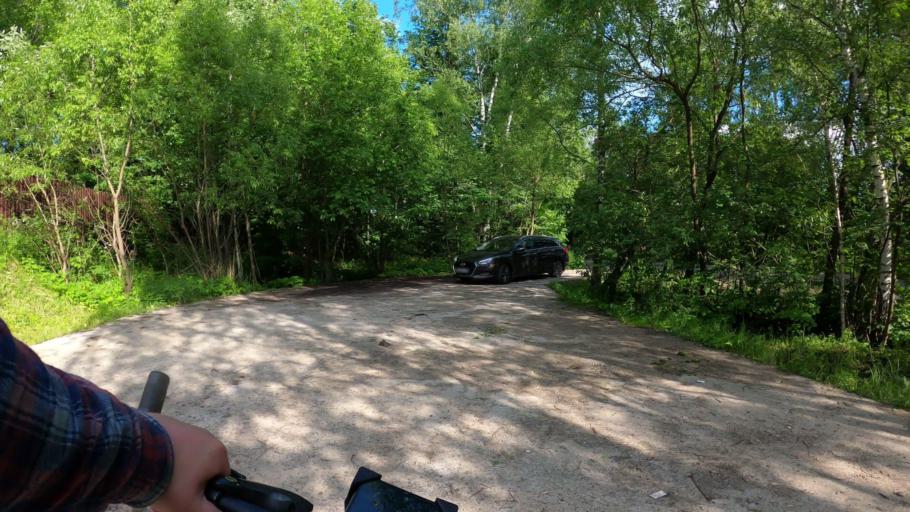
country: RU
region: Moskovskaya
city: Ashitkovo
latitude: 55.4404
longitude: 38.6285
